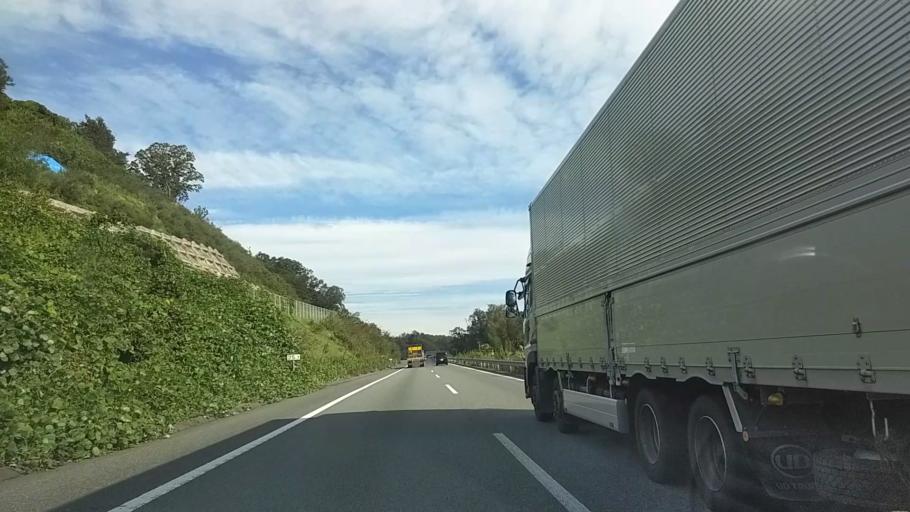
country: JP
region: Kanagawa
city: Zama
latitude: 35.5469
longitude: 139.3194
